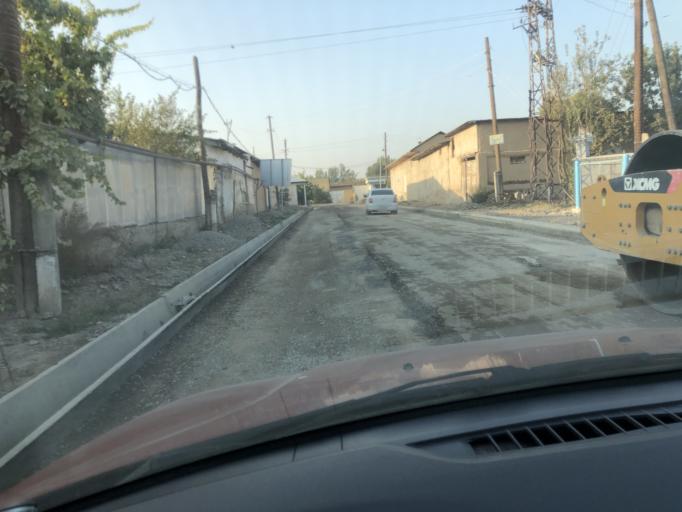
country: UZ
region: Namangan
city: Uychi
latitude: 41.0826
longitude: 71.9991
